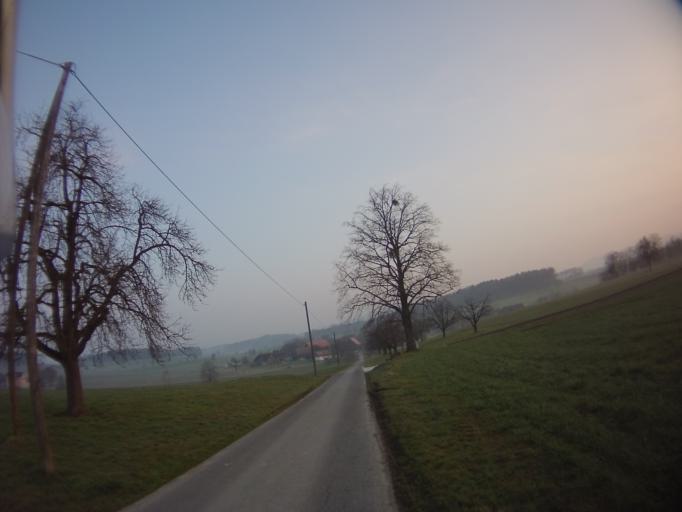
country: CH
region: Zurich
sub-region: Bezirk Affoltern
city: Knonau
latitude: 47.2091
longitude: 8.4494
